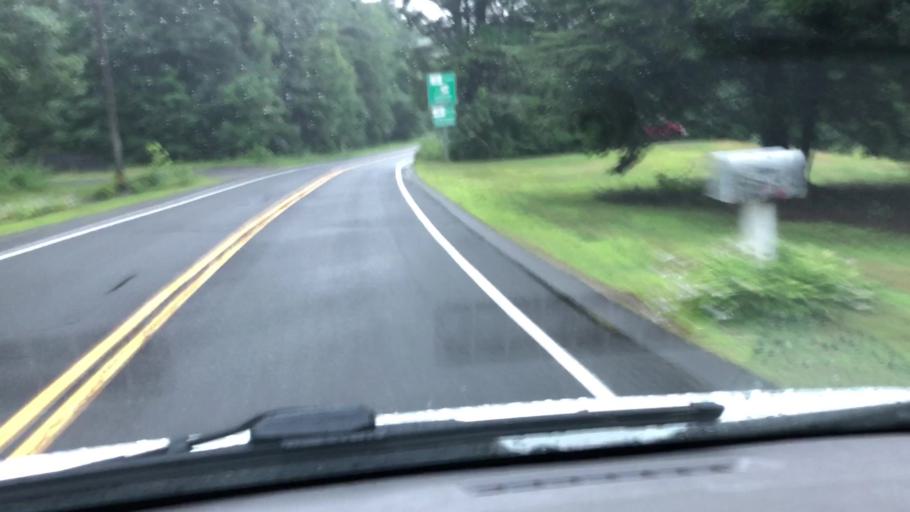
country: US
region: Massachusetts
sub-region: Hampshire County
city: Westhampton
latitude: 42.2784
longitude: -72.8632
